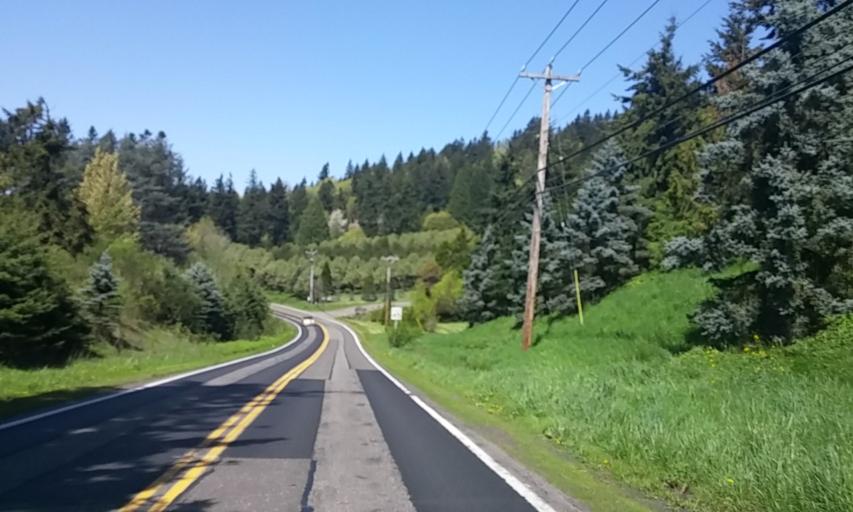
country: US
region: Oregon
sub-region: Washington County
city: West Haven-Sylvan
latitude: 45.5199
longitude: -122.7558
